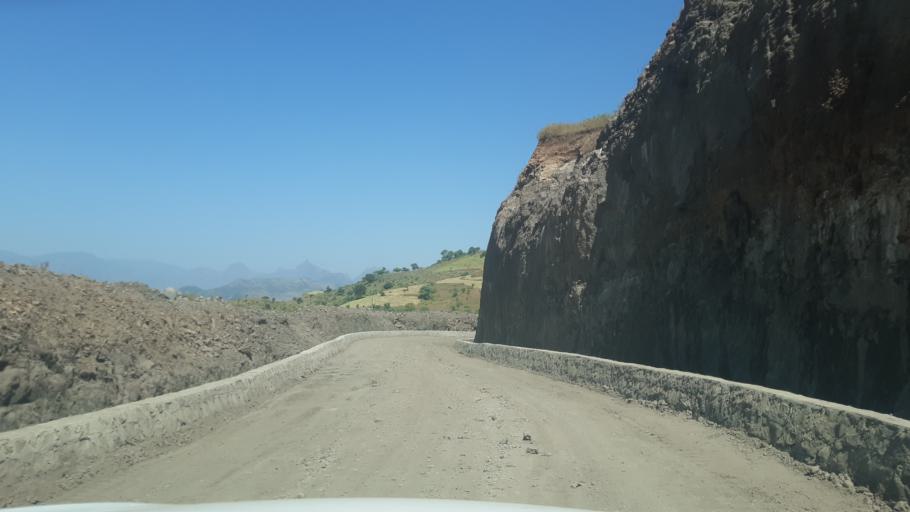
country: ET
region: Amhara
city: Dabat
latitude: 13.1658
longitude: 37.6057
